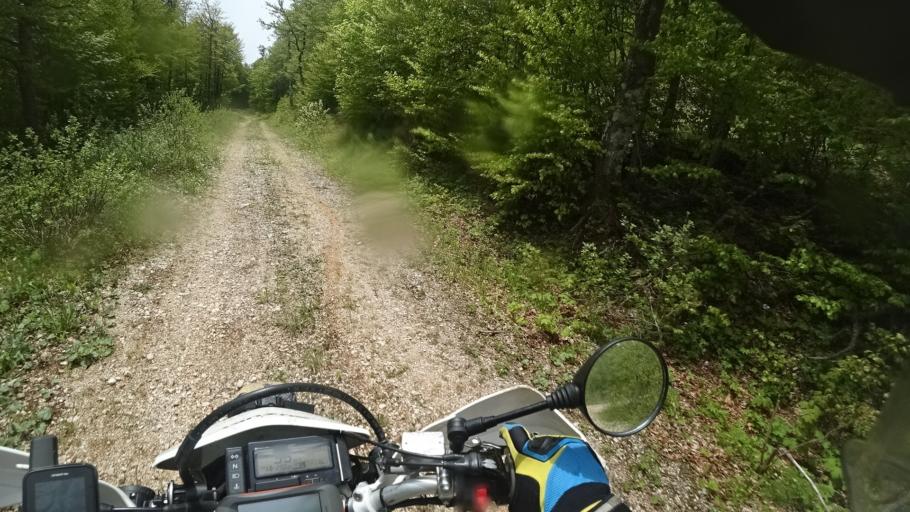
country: BA
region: Federation of Bosnia and Herzegovina
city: Orasac
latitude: 44.5726
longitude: 15.8777
